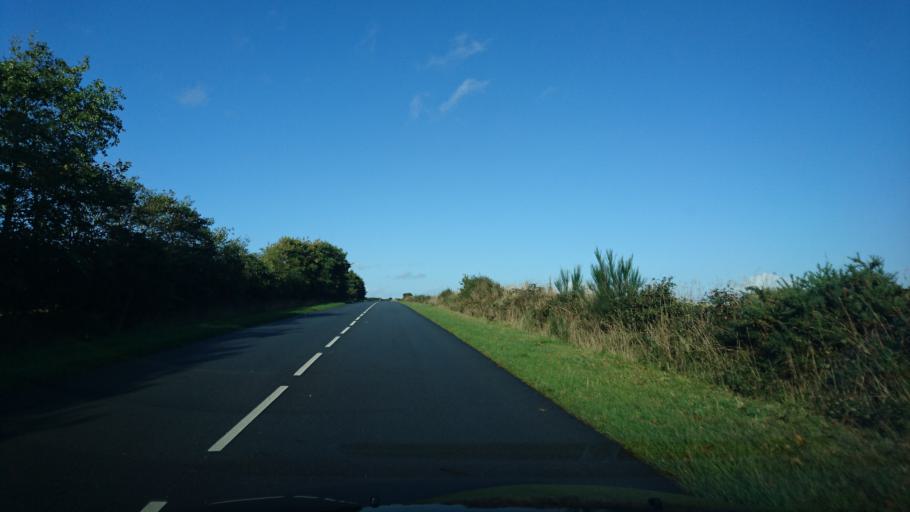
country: FR
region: Brittany
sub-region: Departement du Finistere
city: Plouarzel
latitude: 48.4392
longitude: -4.7339
